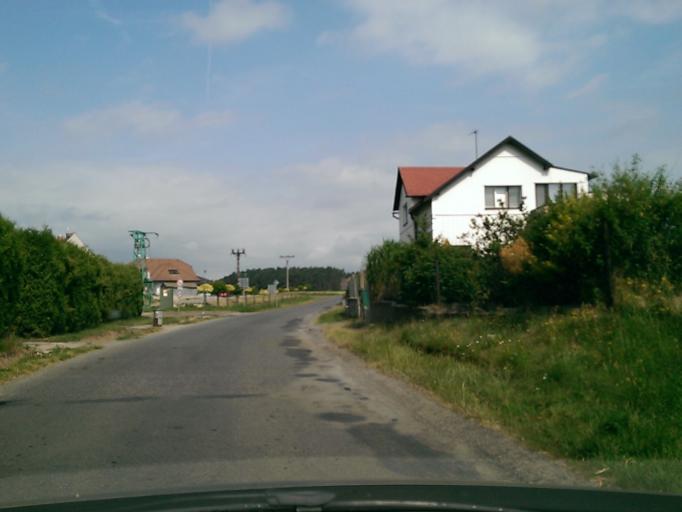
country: CZ
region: Central Bohemia
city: Bela pod Bezdezem
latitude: 50.4756
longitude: 14.8403
